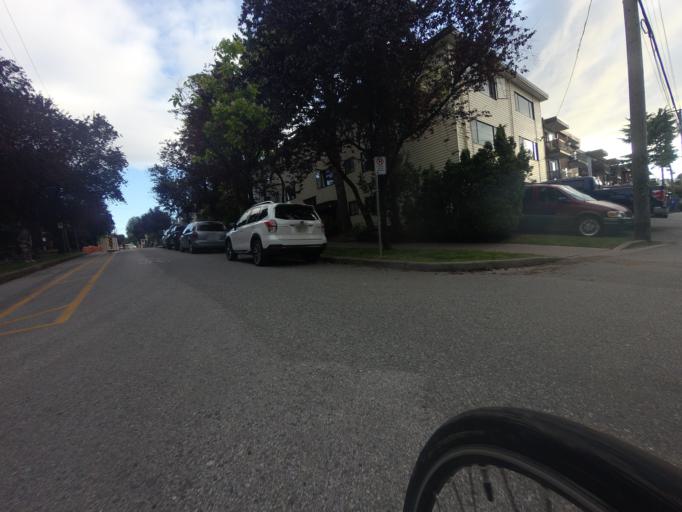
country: CA
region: British Columbia
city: West End
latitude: 49.2694
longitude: -123.1479
